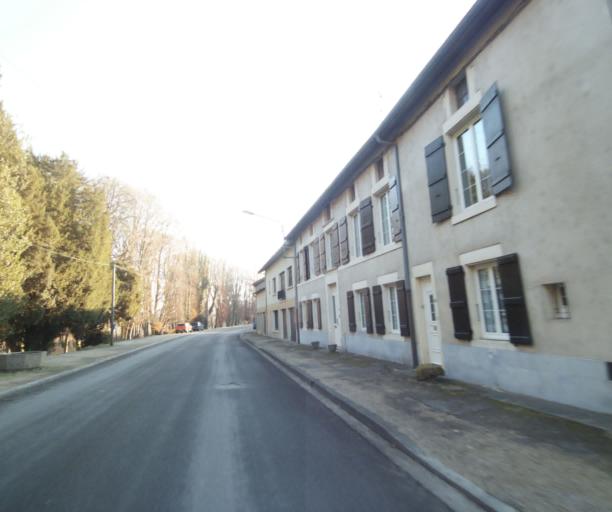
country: FR
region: Champagne-Ardenne
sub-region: Departement de la Haute-Marne
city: Bienville
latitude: 48.5820
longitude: 5.0393
